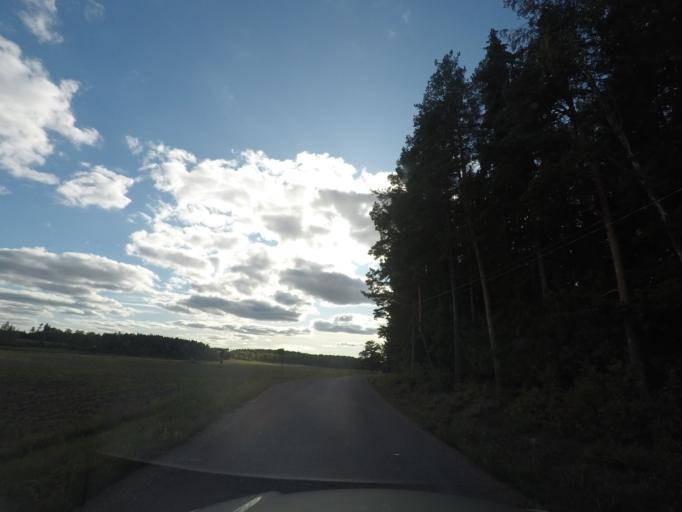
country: SE
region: Vaestmanland
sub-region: Hallstahammars Kommun
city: Kolback
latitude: 59.4899
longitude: 16.1920
